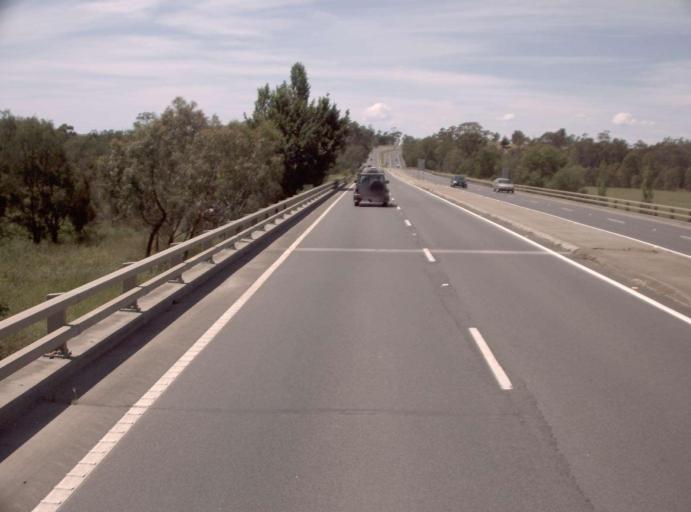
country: AU
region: Victoria
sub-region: Wellington
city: Heyfield
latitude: -38.1460
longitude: 146.7911
